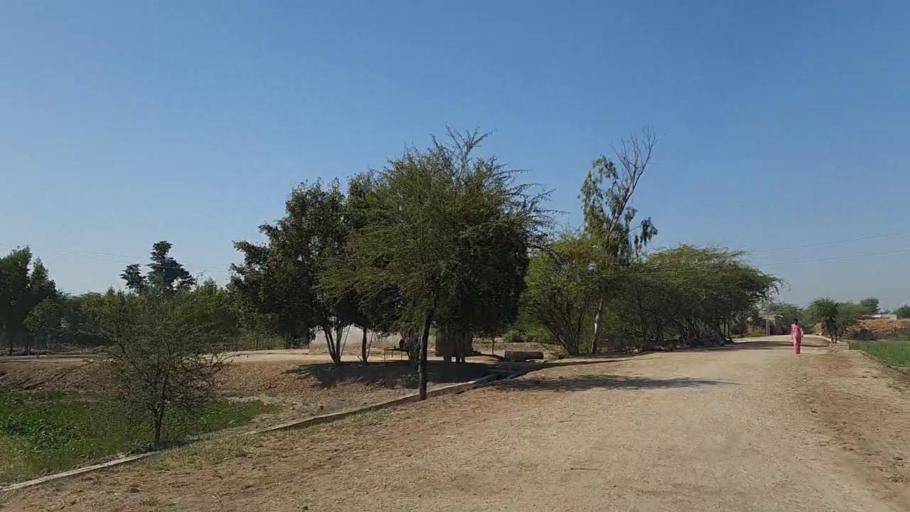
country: PK
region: Sindh
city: Pithoro
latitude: 25.4359
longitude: 69.3720
